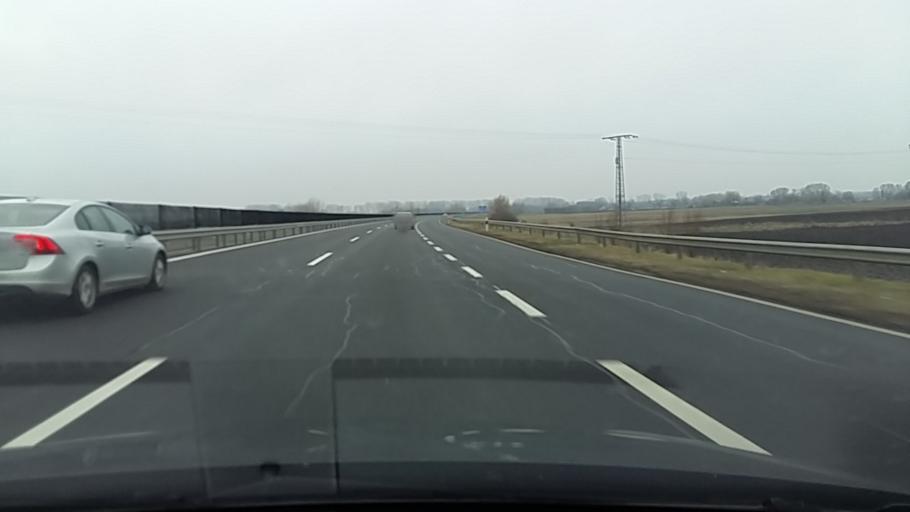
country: HU
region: Szabolcs-Szatmar-Bereg
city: Nyiregyhaza
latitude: 47.8847
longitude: 21.7038
